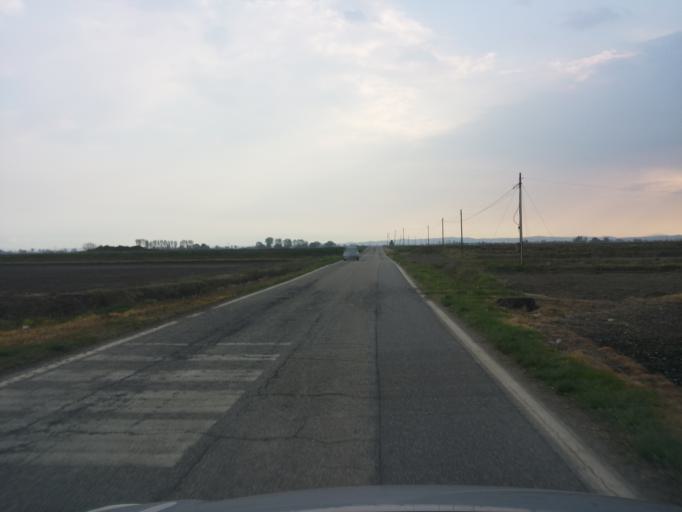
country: IT
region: Piedmont
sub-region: Provincia di Vercelli
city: Caresana
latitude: 45.2136
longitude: 8.5044
